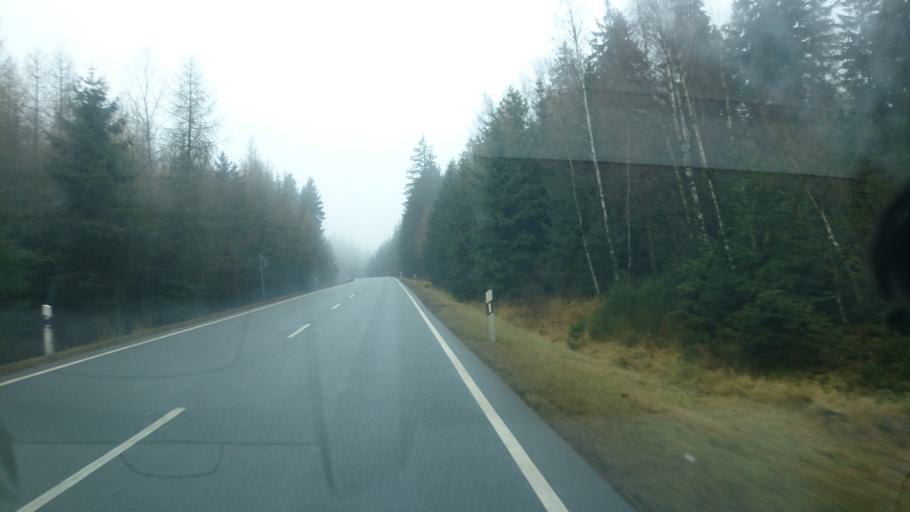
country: DE
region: Thuringia
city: Tanna
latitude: 50.4718
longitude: 11.8405
